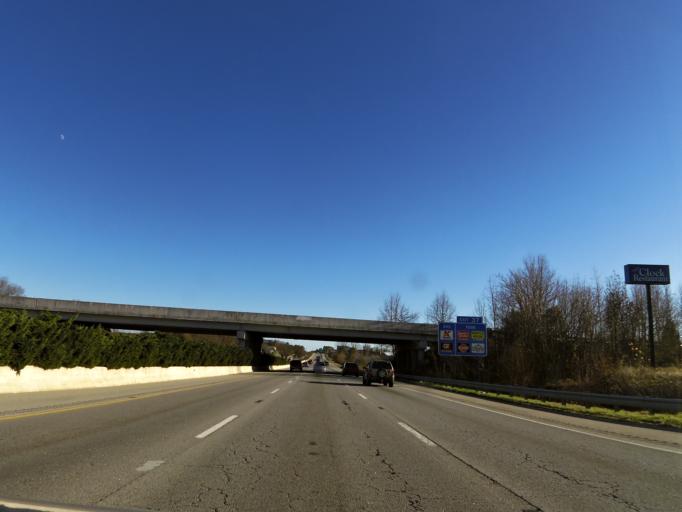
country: US
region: South Carolina
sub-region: Greenville County
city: Wade Hampton
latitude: 34.8486
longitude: -82.3261
